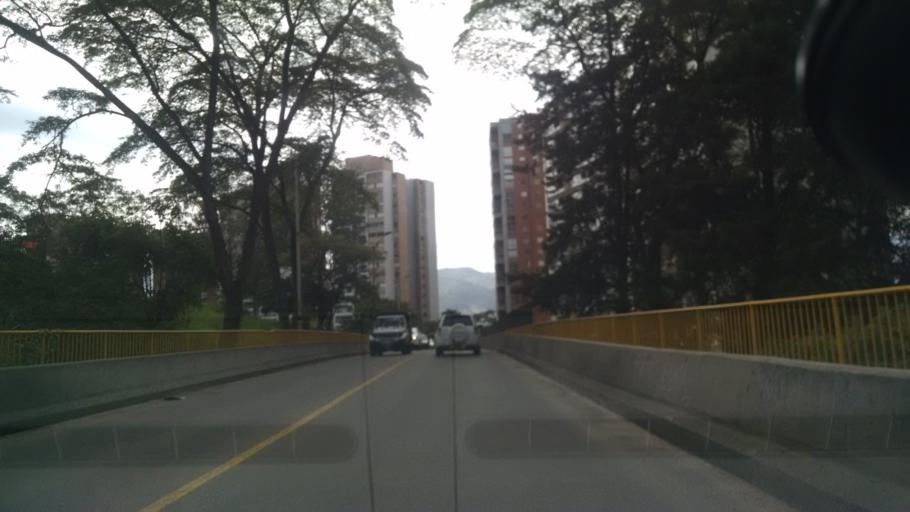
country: CO
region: Antioquia
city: Envigado
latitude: 6.1958
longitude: -75.5692
